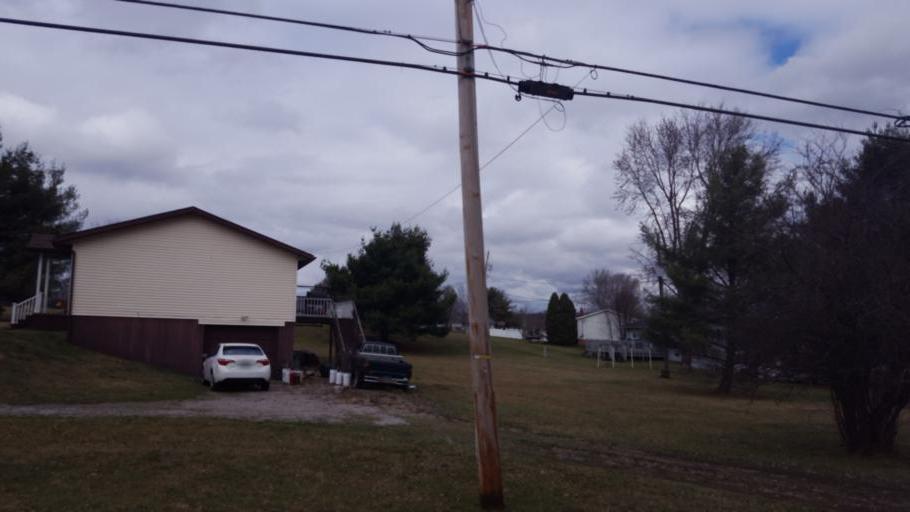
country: US
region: Ohio
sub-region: Muskingum County
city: North Zanesville
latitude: 40.0324
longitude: -82.0502
